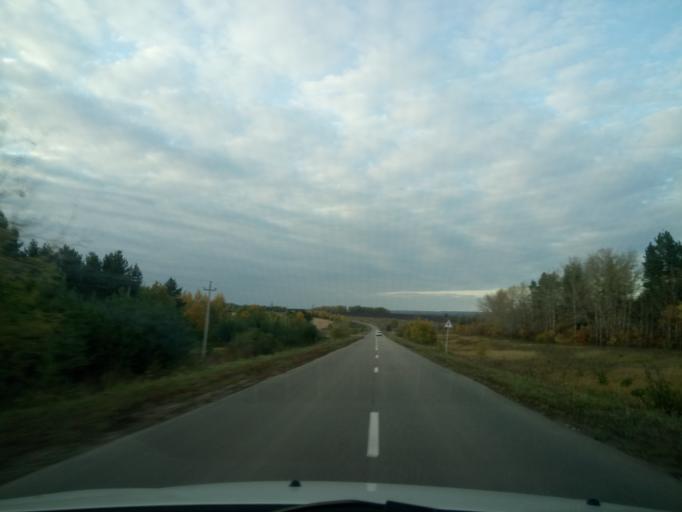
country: RU
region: Nizjnij Novgorod
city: Buturlino
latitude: 55.5321
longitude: 44.9924
